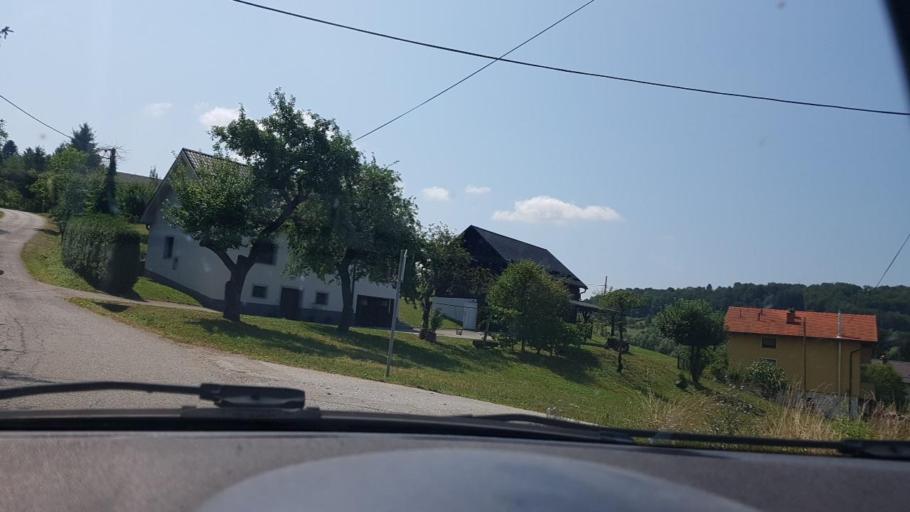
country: SI
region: Rogaska Slatina
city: Rogaska Slatina
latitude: 46.2123
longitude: 15.6462
